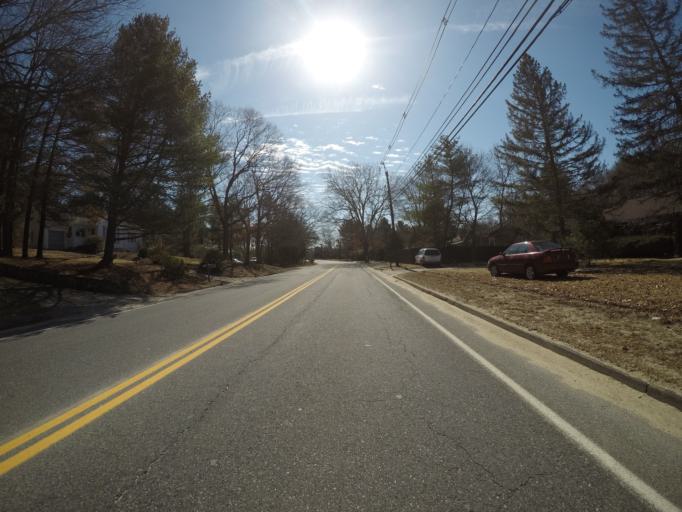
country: US
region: Massachusetts
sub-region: Norfolk County
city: Stoughton
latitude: 42.1102
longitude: -71.1334
